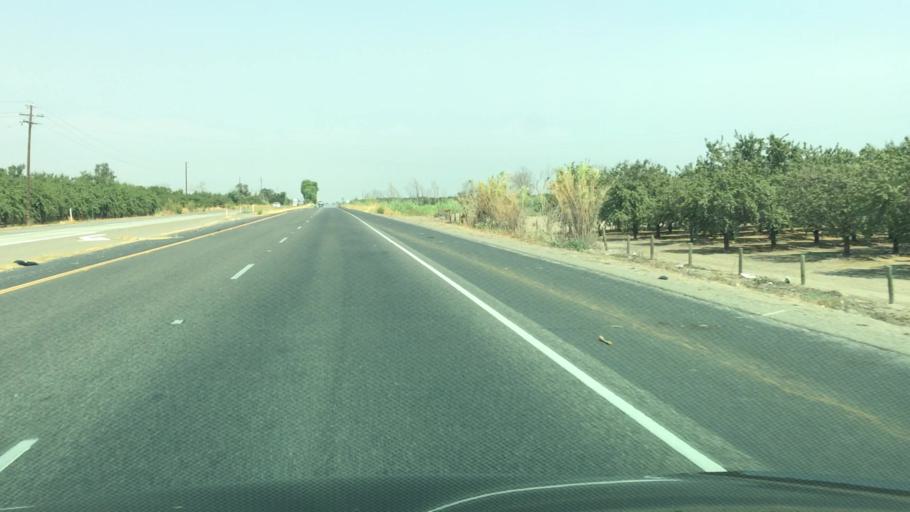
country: US
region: California
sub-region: Madera County
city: Chowchilla
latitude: 37.0835
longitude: -120.2739
